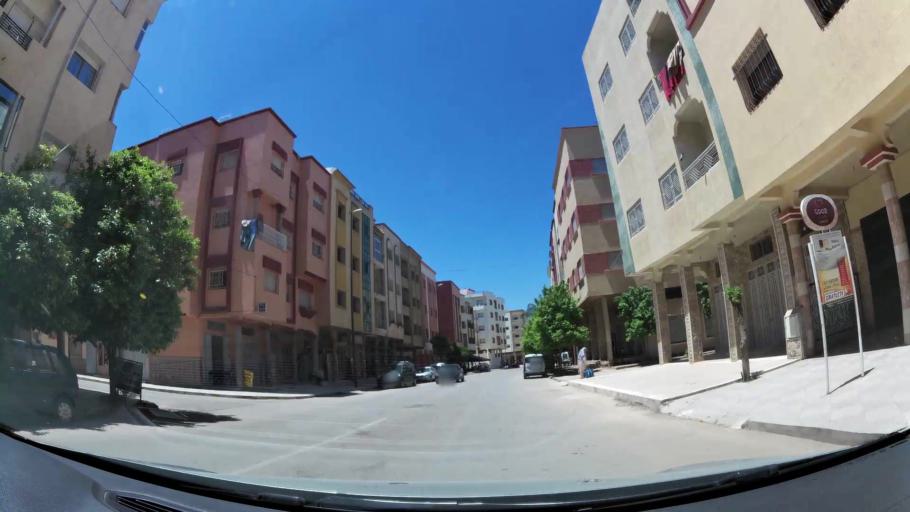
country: MA
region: Meknes-Tafilalet
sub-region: Meknes
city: Meknes
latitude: 33.8601
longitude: -5.5764
